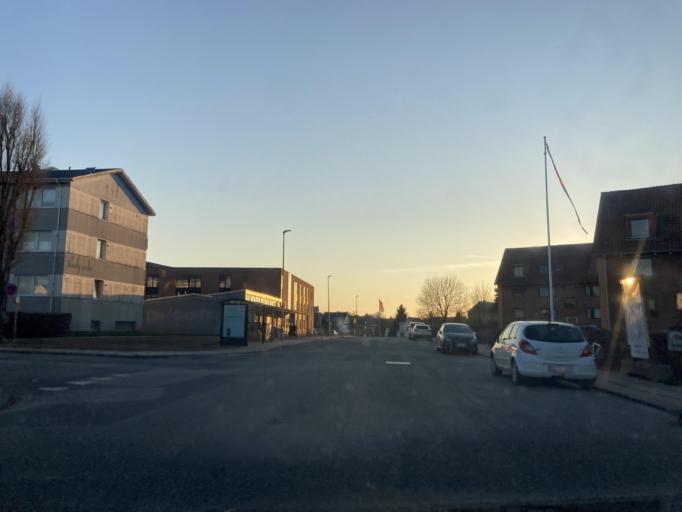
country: DK
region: South Denmark
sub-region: Kolding Kommune
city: Kolding
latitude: 55.4836
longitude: 9.4889
